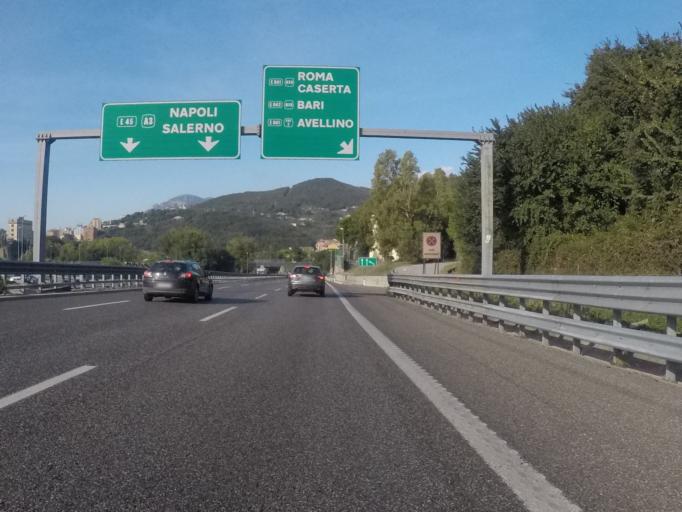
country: IT
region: Campania
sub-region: Provincia di Salerno
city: Capezzano Inferiore
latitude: 40.6971
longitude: 14.7864
